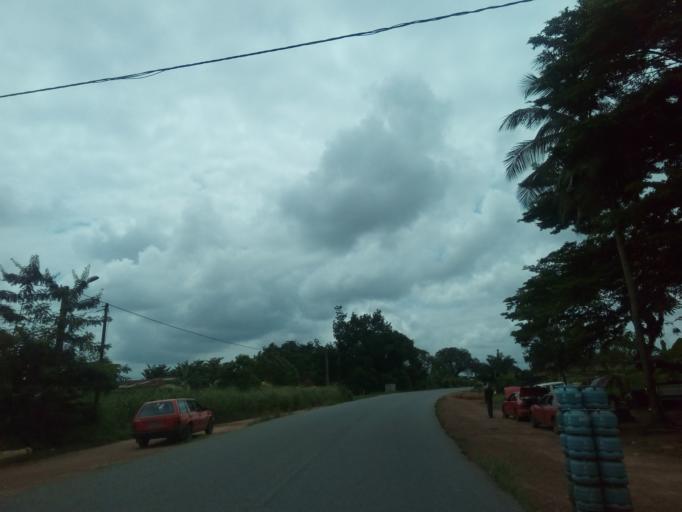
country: CI
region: Sud-Comoe
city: Aboisso
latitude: 5.4551
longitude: -3.2576
